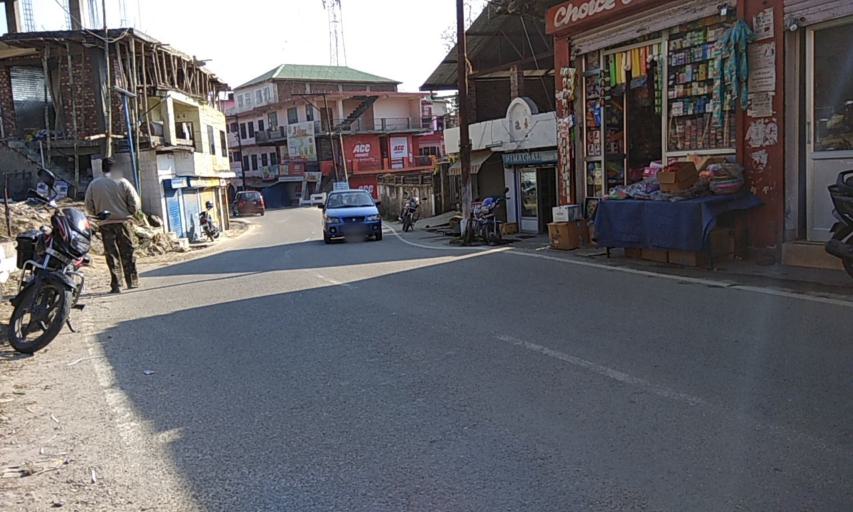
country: IN
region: Himachal Pradesh
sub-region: Kangra
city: Palampur
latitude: 32.1128
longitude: 76.5298
